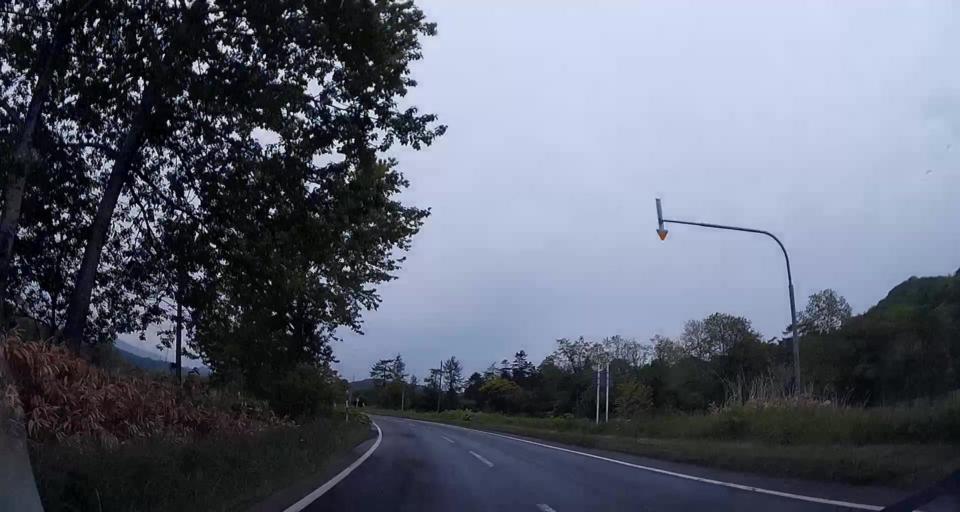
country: JP
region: Hokkaido
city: Shiraoi
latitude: 42.5763
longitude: 141.3244
